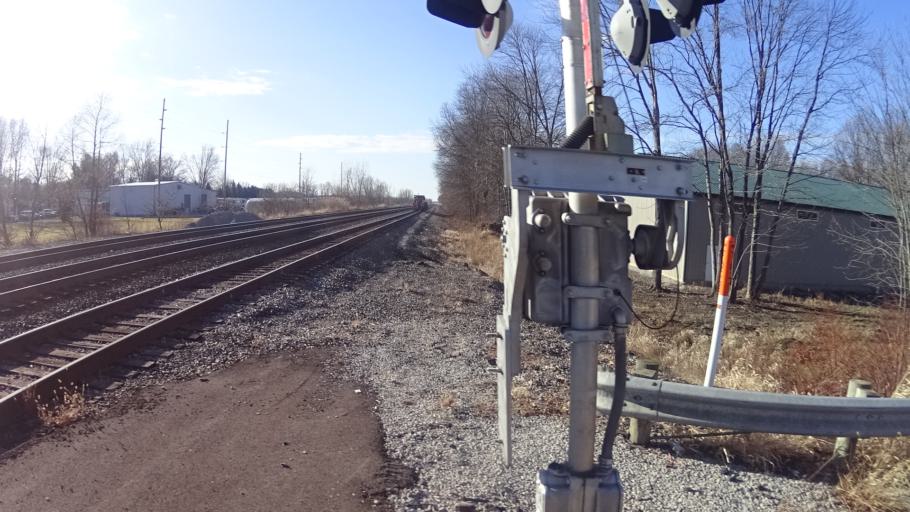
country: US
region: Ohio
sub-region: Lorain County
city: North Ridgeville
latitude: 41.3757
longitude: -82.0319
